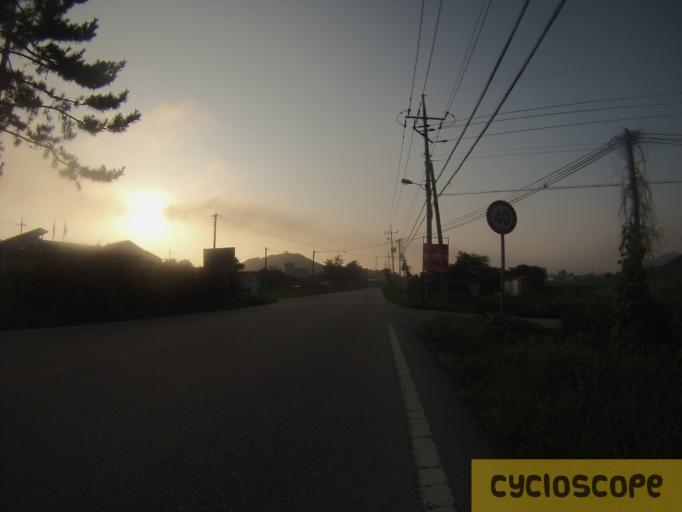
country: KR
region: Jeollabuk-do
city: Puan
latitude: 35.6280
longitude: 126.4707
